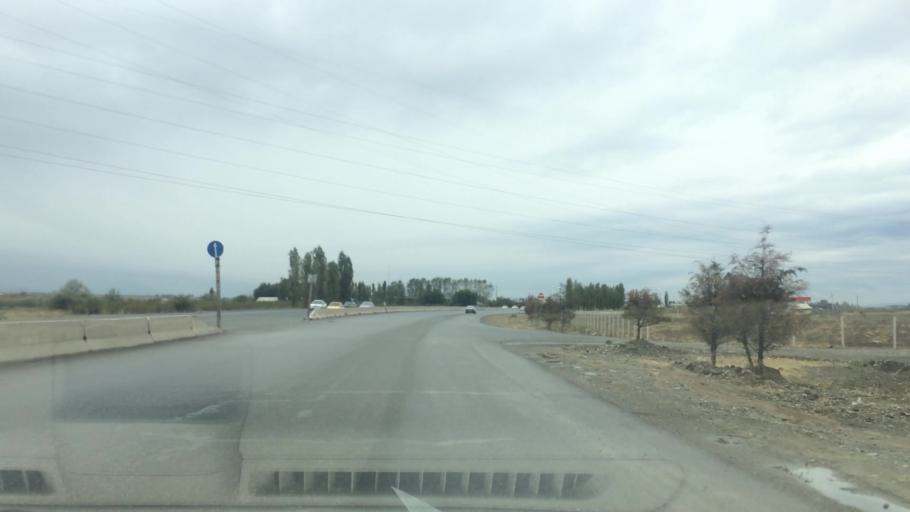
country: UZ
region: Jizzax
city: Jizzax
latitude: 40.0250
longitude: 67.6155
